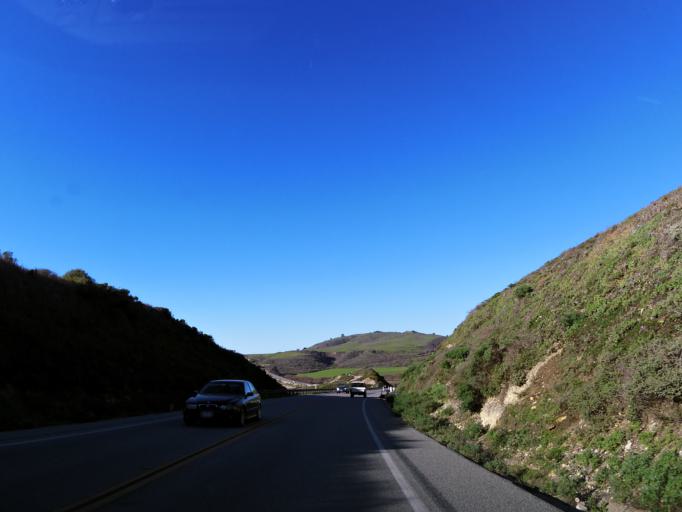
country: US
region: California
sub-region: Santa Cruz County
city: Bonny Doon
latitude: 37.0354
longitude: -122.2260
